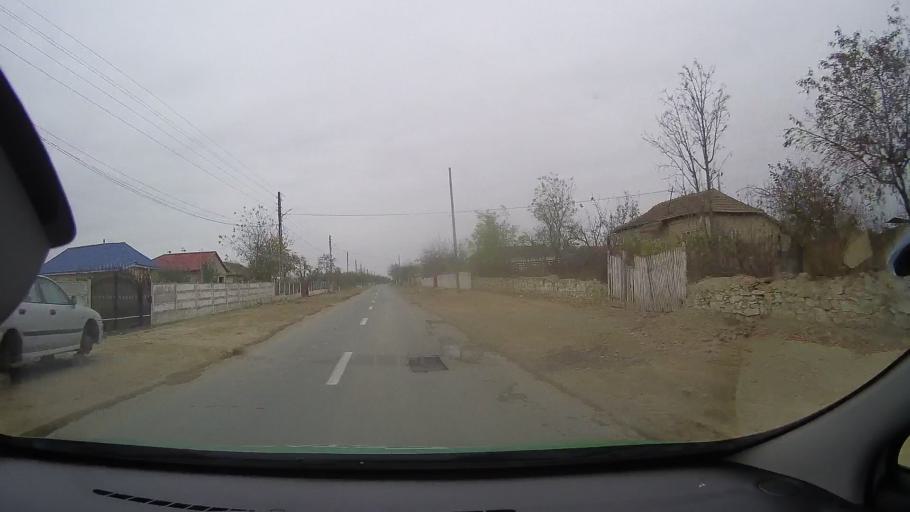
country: RO
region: Constanta
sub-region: Comuna Vulturu
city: Vulturu
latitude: 44.6406
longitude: 28.2743
